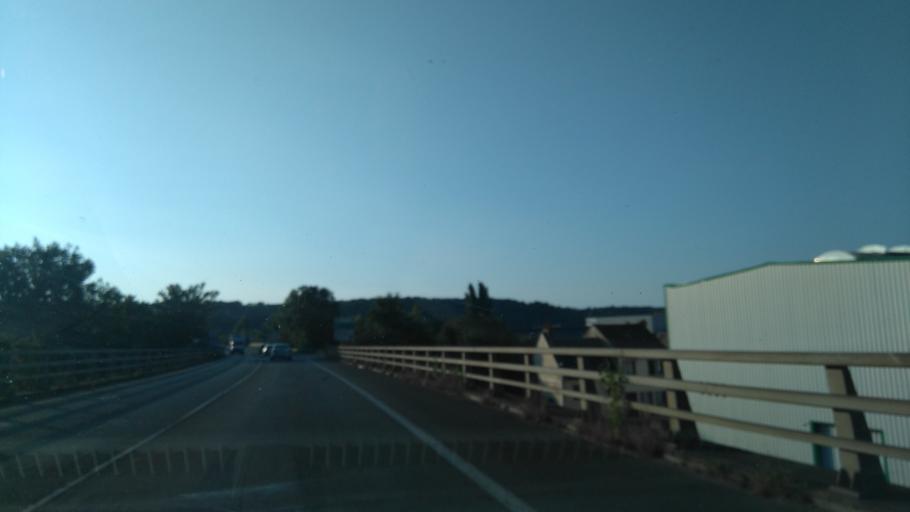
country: FR
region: Picardie
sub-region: Departement de l'Oise
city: Montataire
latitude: 49.2534
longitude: 2.4559
